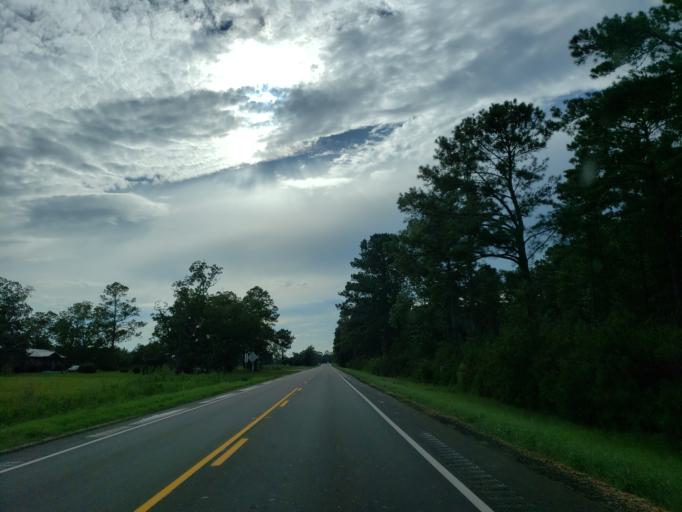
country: US
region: Georgia
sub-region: Irwin County
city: Ocilla
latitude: 31.5635
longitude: -83.3306
